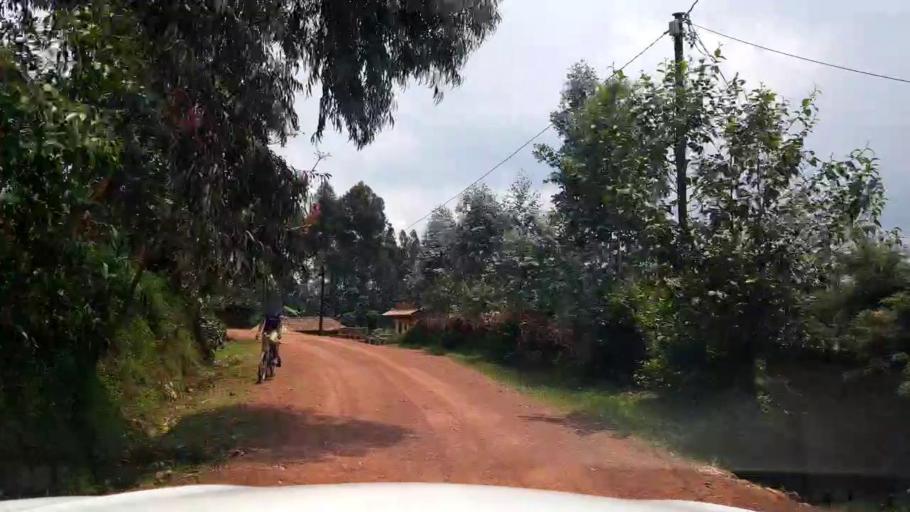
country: RW
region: Northern Province
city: Byumba
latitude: -1.4941
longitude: 29.9296
